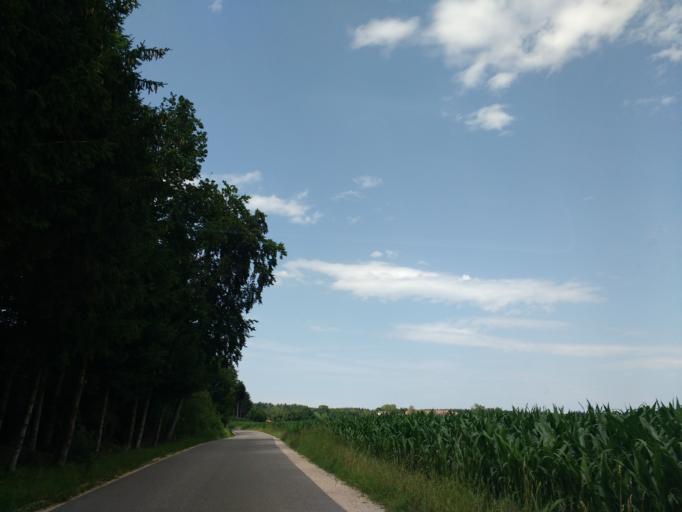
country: DE
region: Bavaria
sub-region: Upper Bavaria
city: Seeon-Seebruck
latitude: 47.9924
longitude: 12.4486
